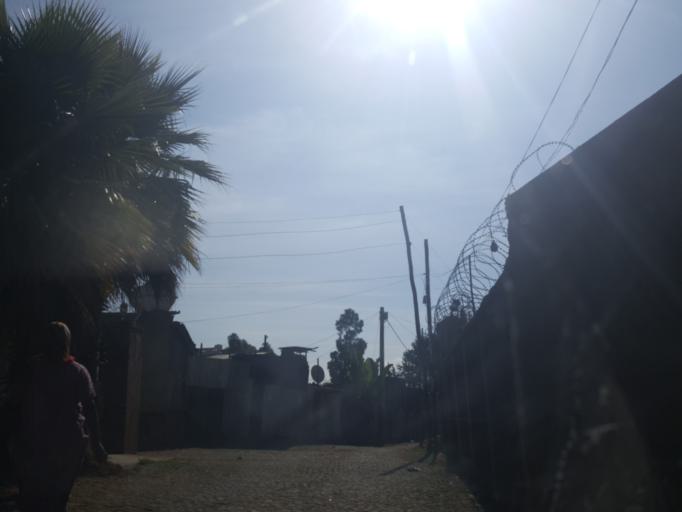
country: ET
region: Adis Abeba
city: Addis Ababa
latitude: 9.0557
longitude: 38.7269
